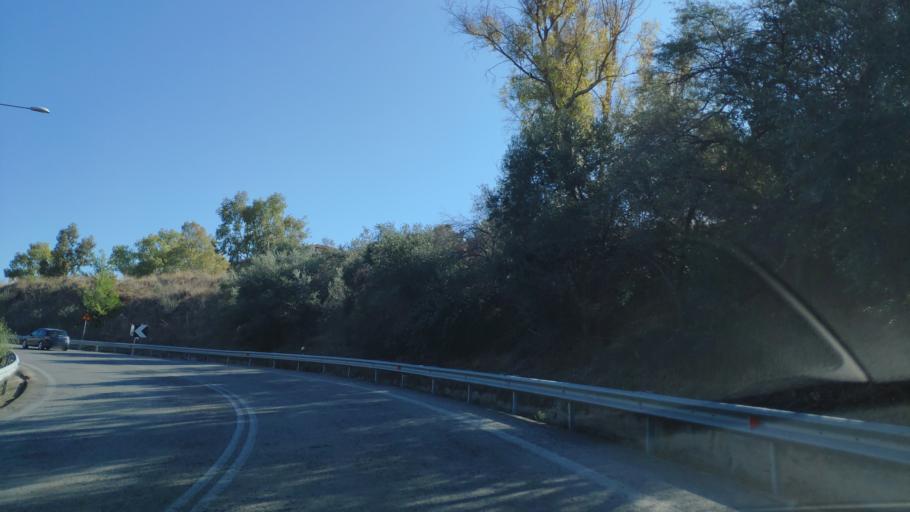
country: GR
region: Peloponnese
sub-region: Nomos Korinthias
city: Arkhaia Korinthos
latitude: 37.9133
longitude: 22.8859
